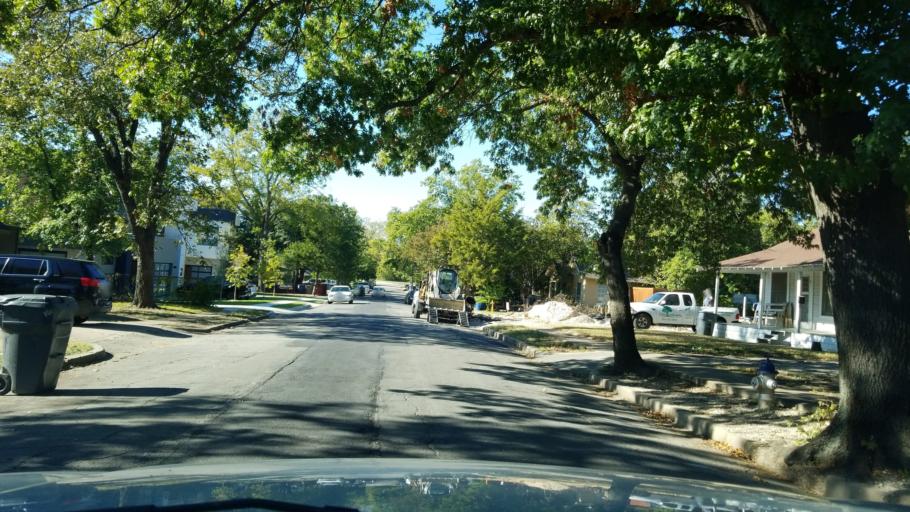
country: US
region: Texas
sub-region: Dallas County
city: Highland Park
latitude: 32.8034
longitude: -96.7461
